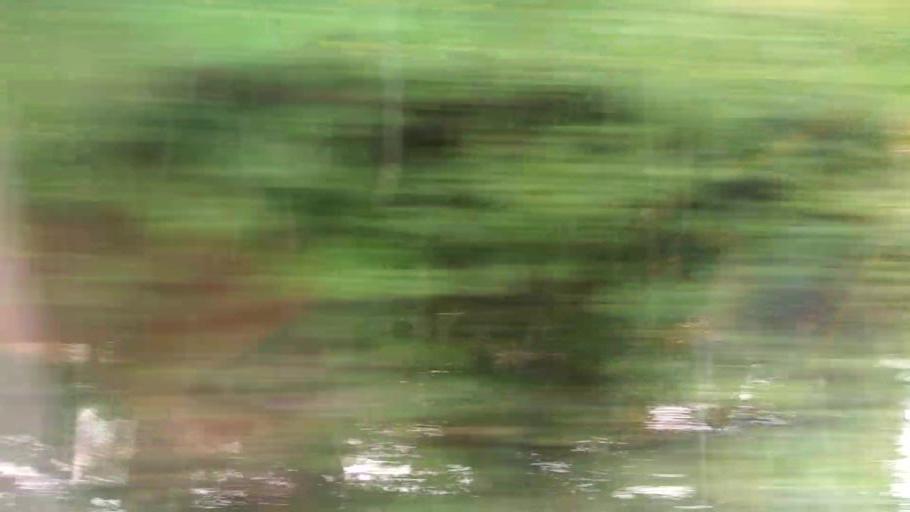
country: RU
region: Moskovskaya
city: Lukhovitsy
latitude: 54.9319
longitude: 39.0037
